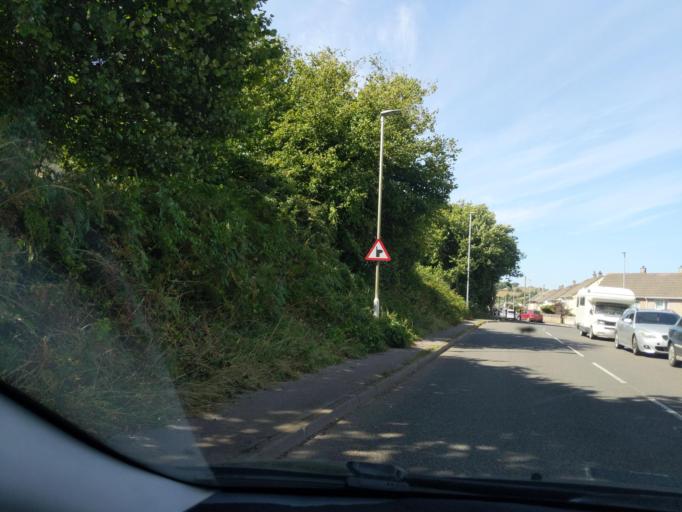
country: GB
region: England
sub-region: Devon
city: Plympton
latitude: 50.3786
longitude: -4.0382
